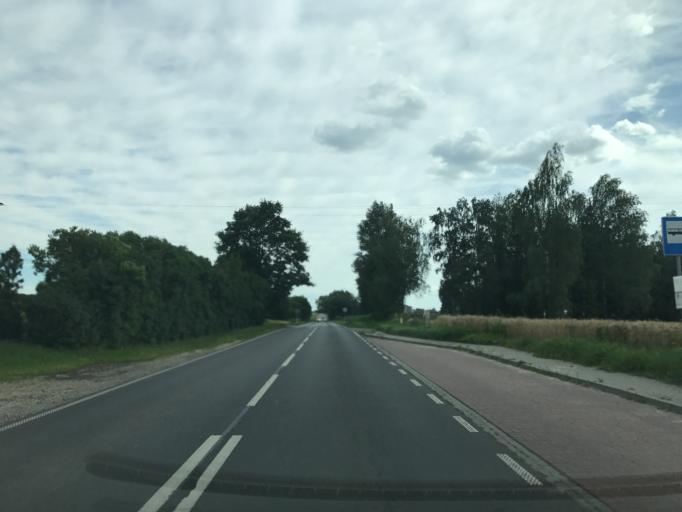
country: PL
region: Kujawsko-Pomorskie
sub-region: Powiat brodnicki
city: Brodnica
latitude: 53.2159
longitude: 19.3852
